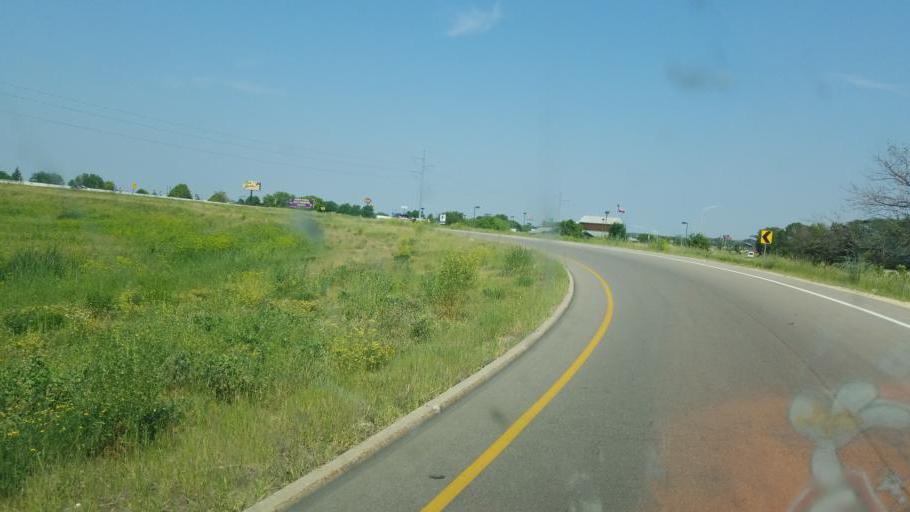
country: US
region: Wisconsin
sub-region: Rock County
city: Janesville
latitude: 42.7181
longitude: -88.9824
